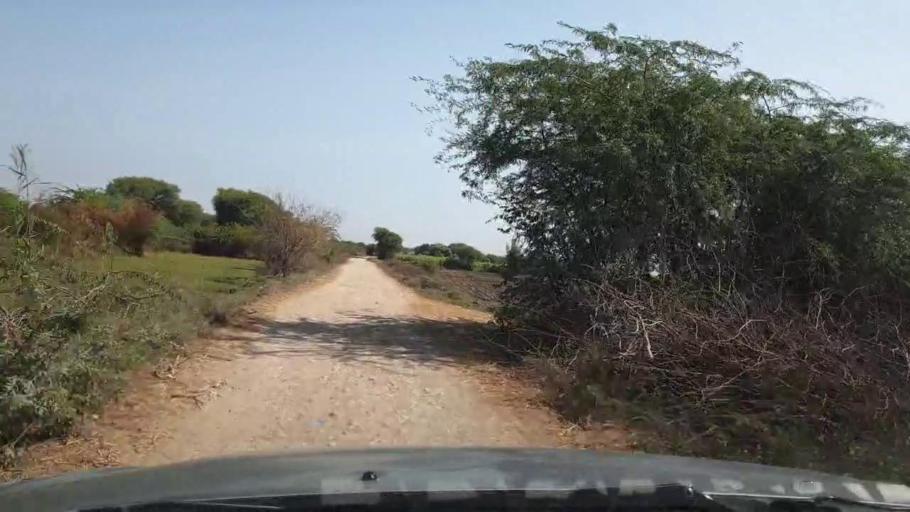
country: PK
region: Sindh
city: Bulri
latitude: 25.0228
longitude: 68.3037
